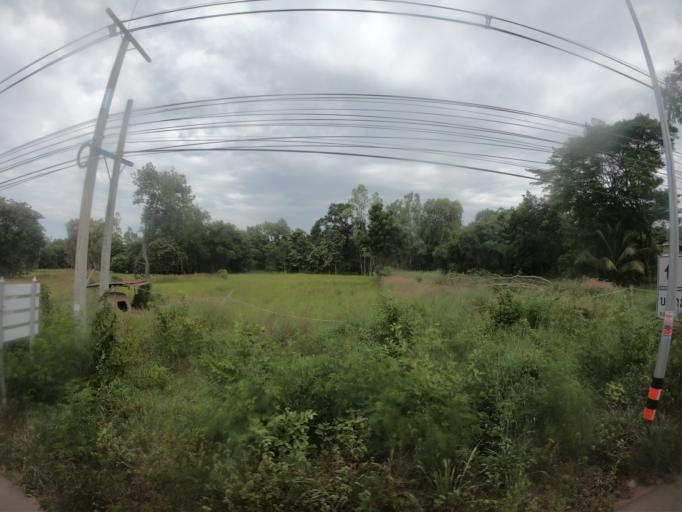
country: TH
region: Maha Sarakham
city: Kantharawichai
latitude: 16.3384
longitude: 103.1880
